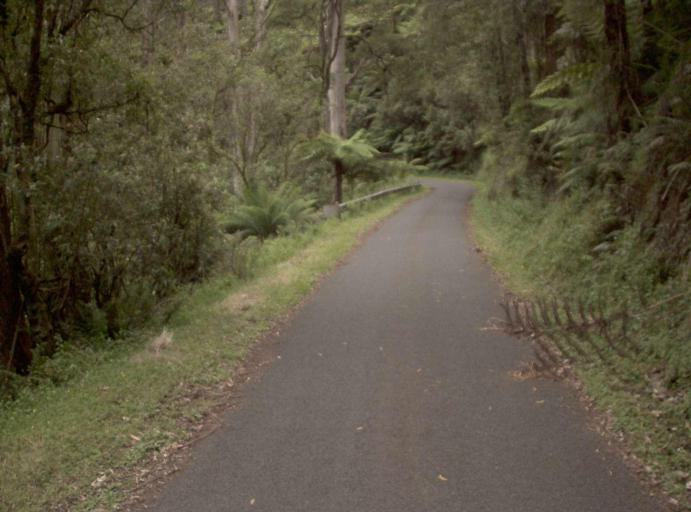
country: AU
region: Victoria
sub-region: Latrobe
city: Traralgon
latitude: -38.4607
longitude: 146.5481
